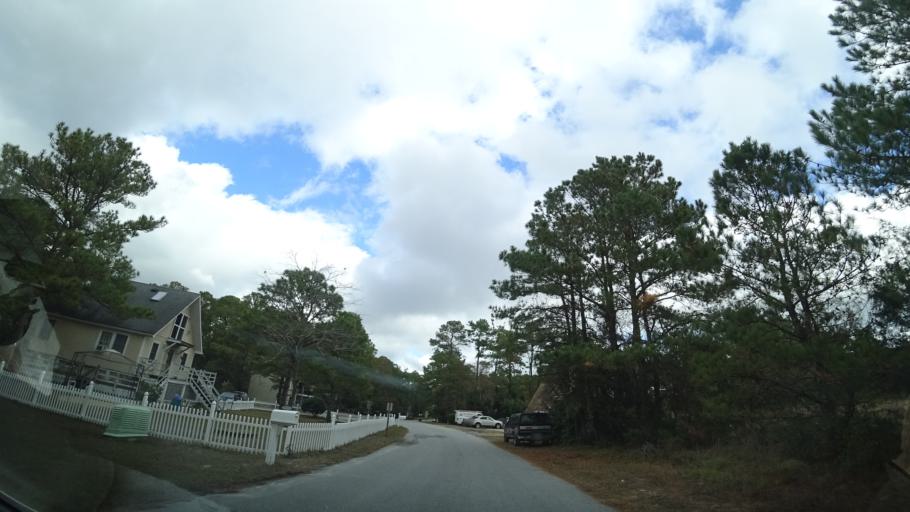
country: US
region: North Carolina
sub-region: Dare County
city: Kill Devil Hills
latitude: 35.9913
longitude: -75.6599
